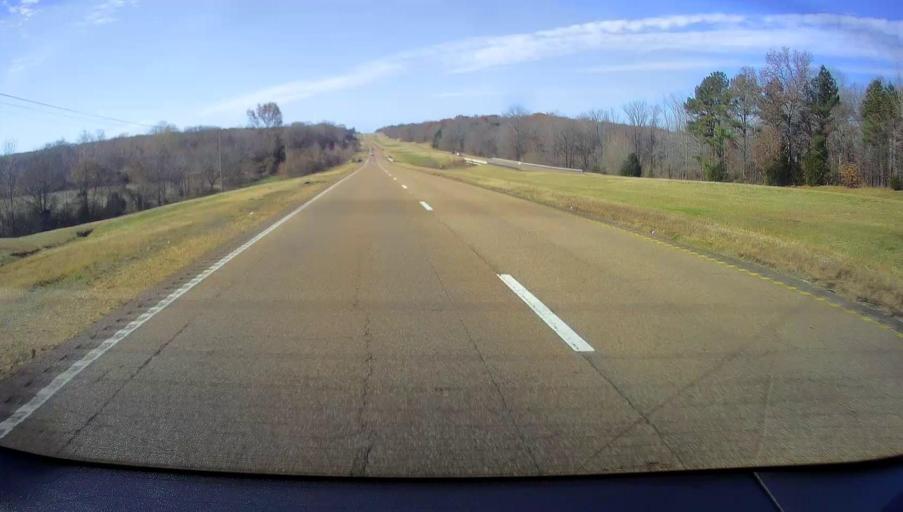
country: US
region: Mississippi
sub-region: Marshall County
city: Holly Springs
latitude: 34.9464
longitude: -89.4127
